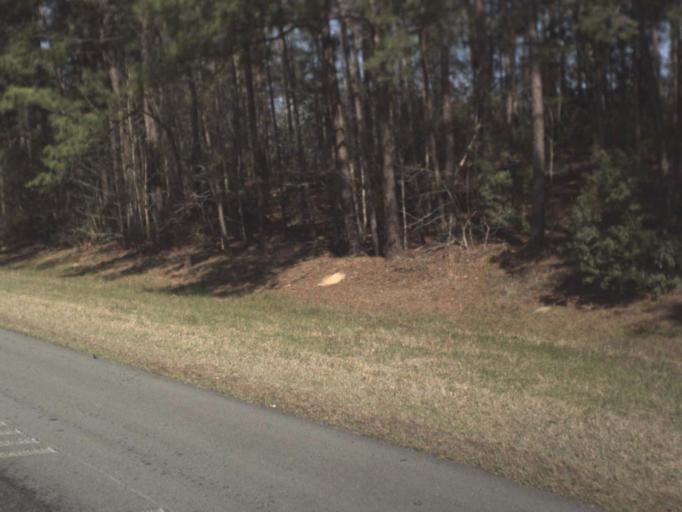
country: US
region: Florida
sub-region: Gadsden County
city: Chattahoochee
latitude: 30.6189
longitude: -84.8329
